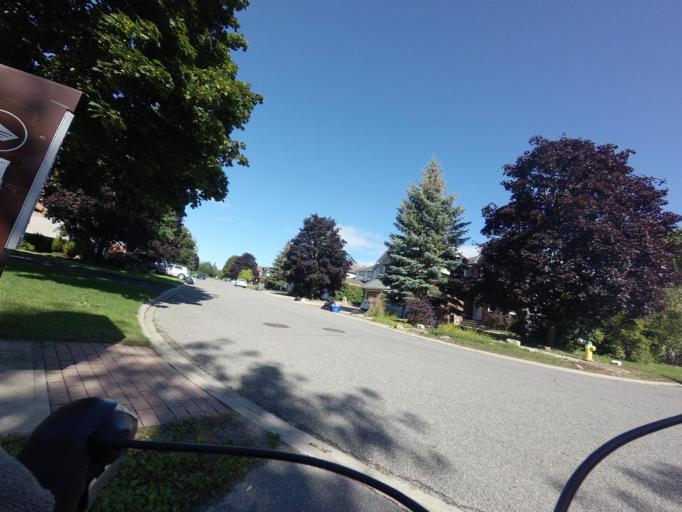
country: CA
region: Ontario
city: Bells Corners
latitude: 45.3124
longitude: -75.8343
